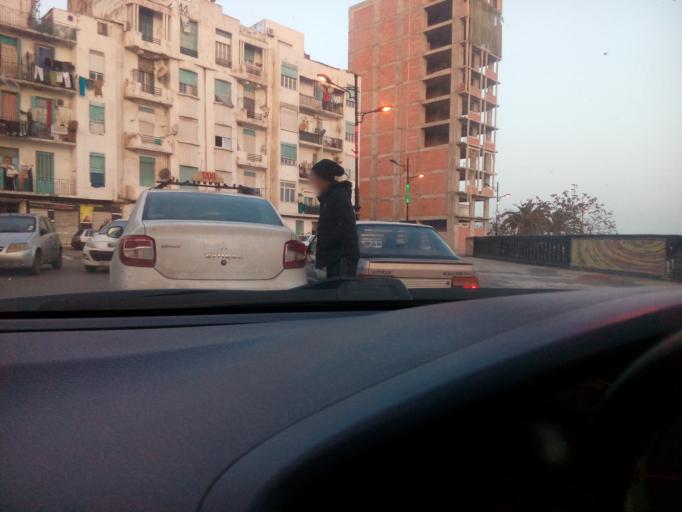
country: DZ
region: Oran
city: Oran
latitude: 35.7054
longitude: -0.6424
